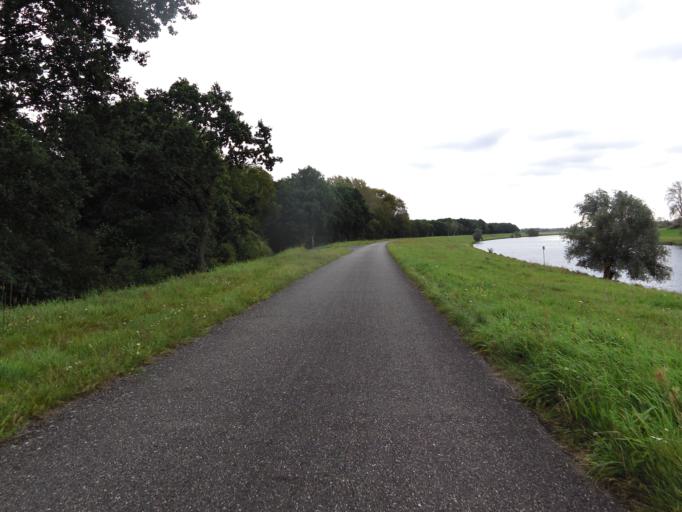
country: DE
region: Brandenburg
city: Bad Wilsnack
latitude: 52.8887
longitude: 11.9608
